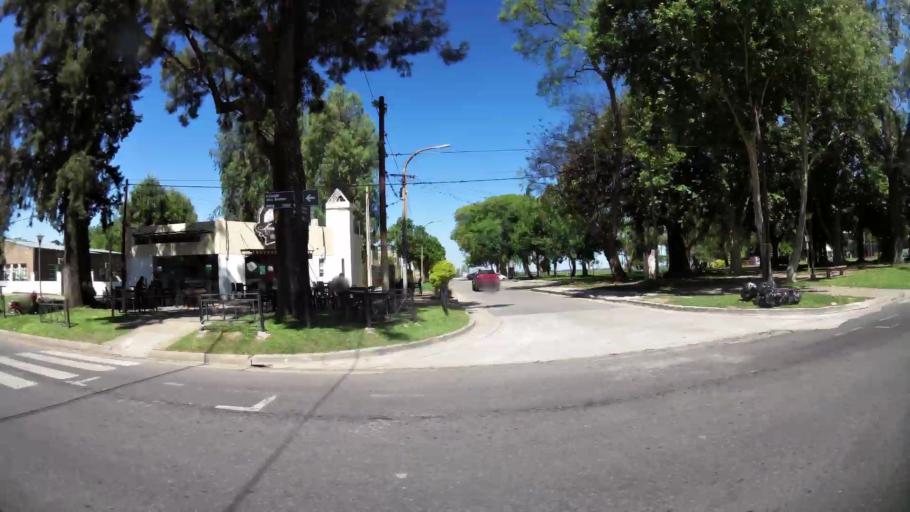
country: AR
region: Santa Fe
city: Santa Fe de la Vera Cruz
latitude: -31.6068
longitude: -60.6662
